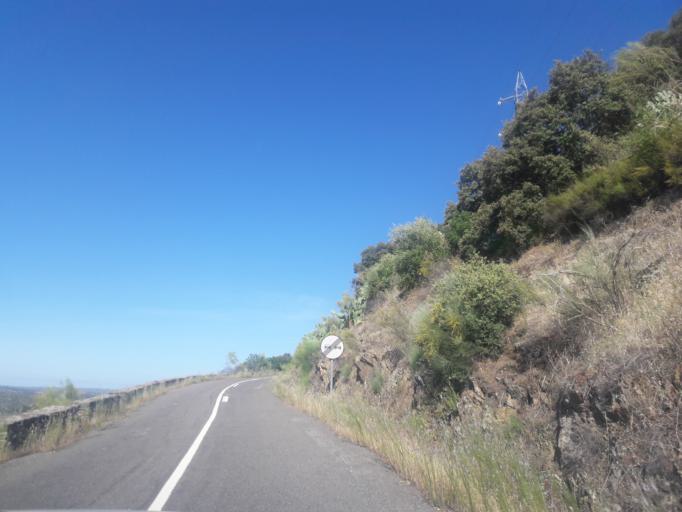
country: ES
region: Castille and Leon
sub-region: Provincia de Salamanca
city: Saucelle
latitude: 41.0326
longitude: -6.7651
